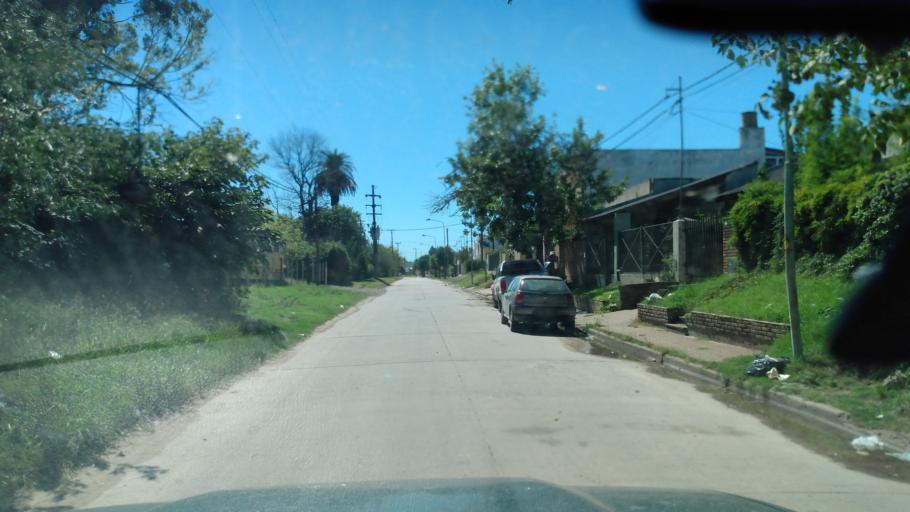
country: AR
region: Buenos Aires
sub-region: Partido de Lujan
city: Lujan
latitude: -34.5740
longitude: -59.1254
